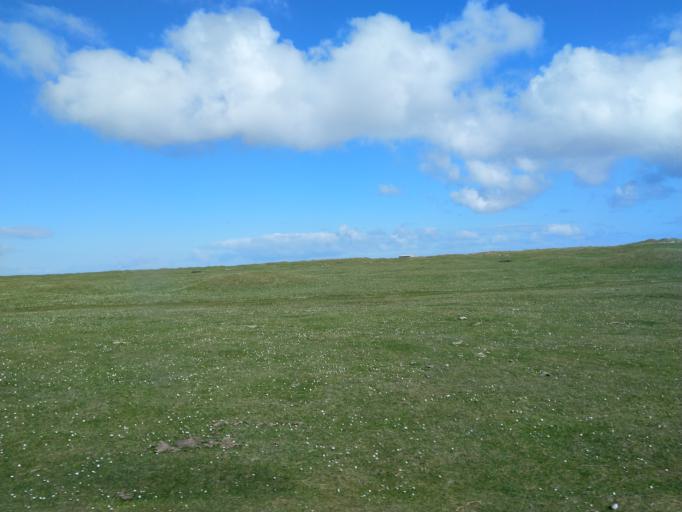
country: GB
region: Scotland
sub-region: Eilean Siar
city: Barra
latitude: 56.4766
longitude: -6.9765
